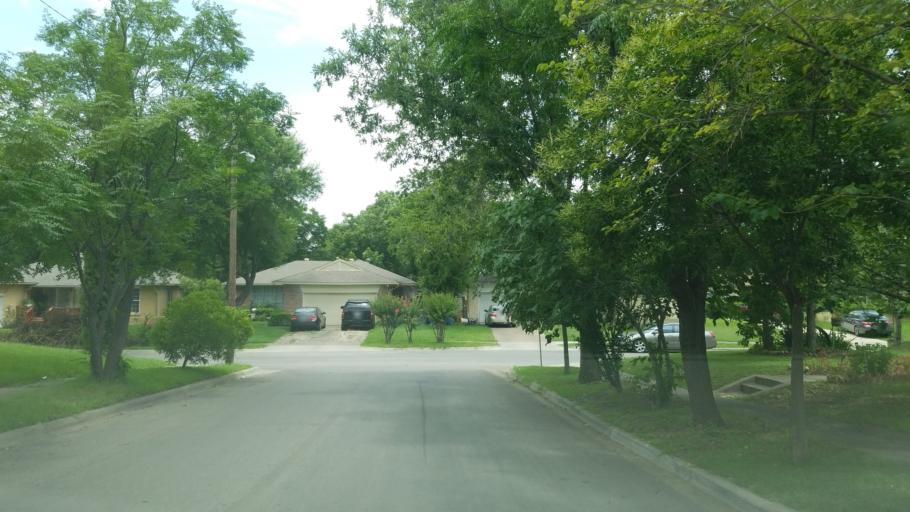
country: US
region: Texas
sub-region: Dallas County
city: Farmers Branch
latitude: 32.8923
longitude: -96.8780
